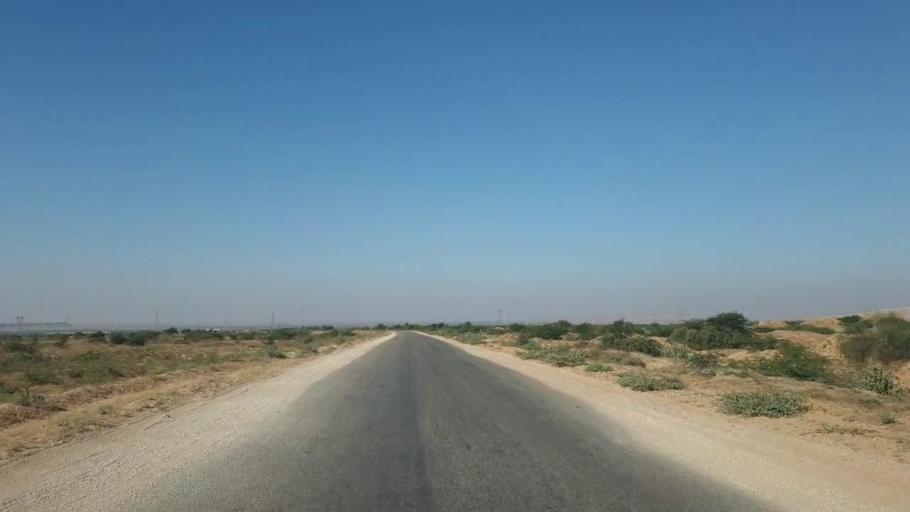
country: PK
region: Sindh
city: Gharo
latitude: 25.1646
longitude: 67.6624
